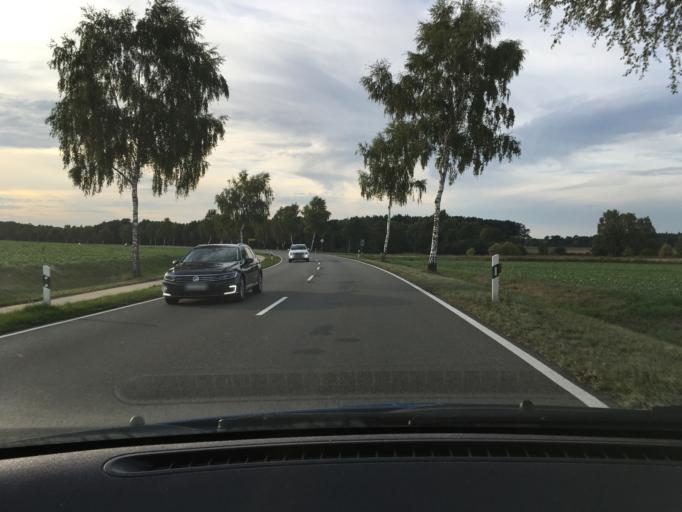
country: DE
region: Lower Saxony
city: Soltau
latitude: 53.0110
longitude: 9.9030
